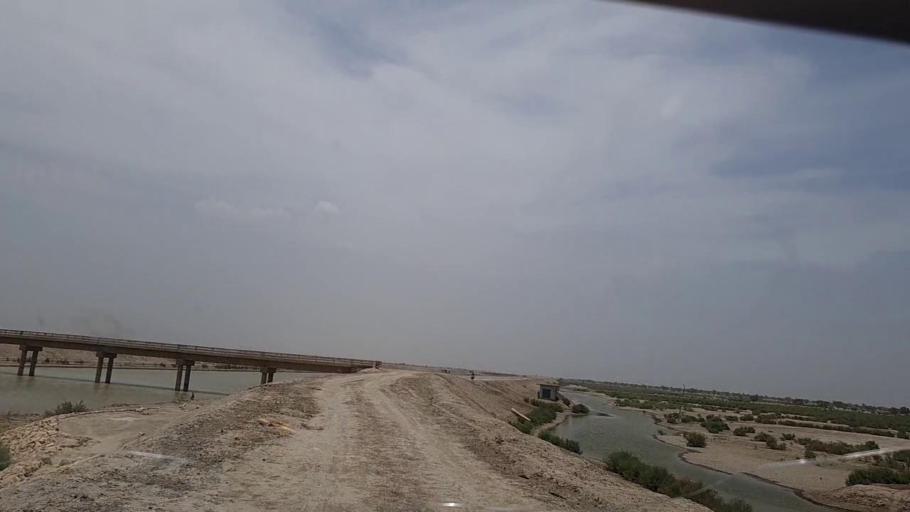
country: PK
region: Sindh
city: Bhan
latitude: 26.5099
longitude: 67.6255
